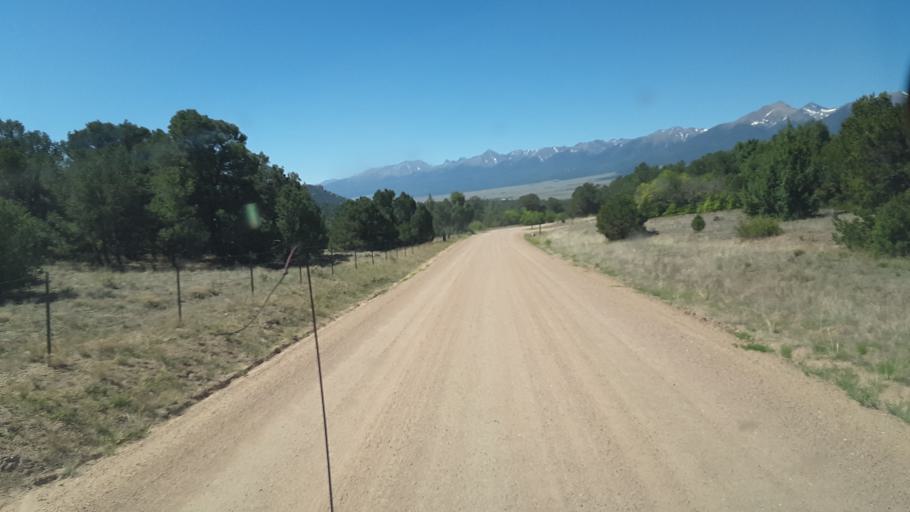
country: US
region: Colorado
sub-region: Custer County
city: Westcliffe
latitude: 38.2644
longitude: -105.5467
